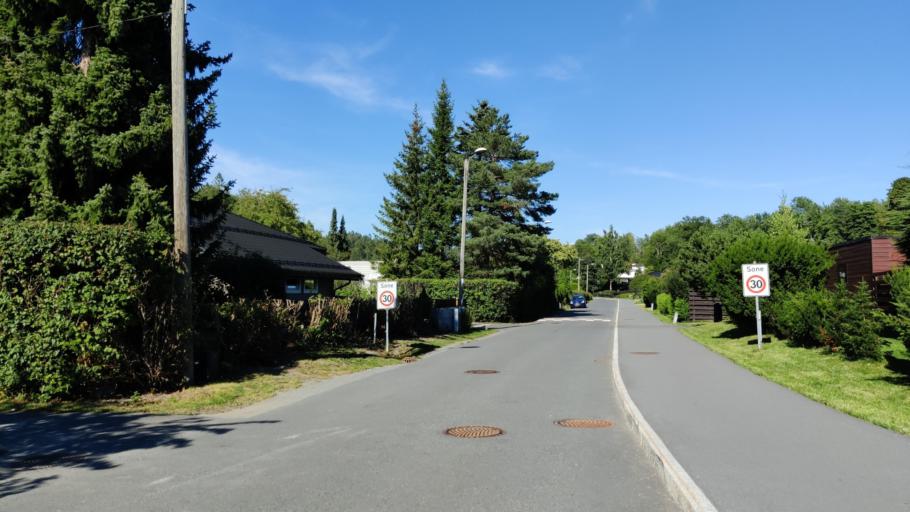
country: NO
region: Akershus
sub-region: Baerum
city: Lysaker
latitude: 59.9282
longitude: 10.6007
